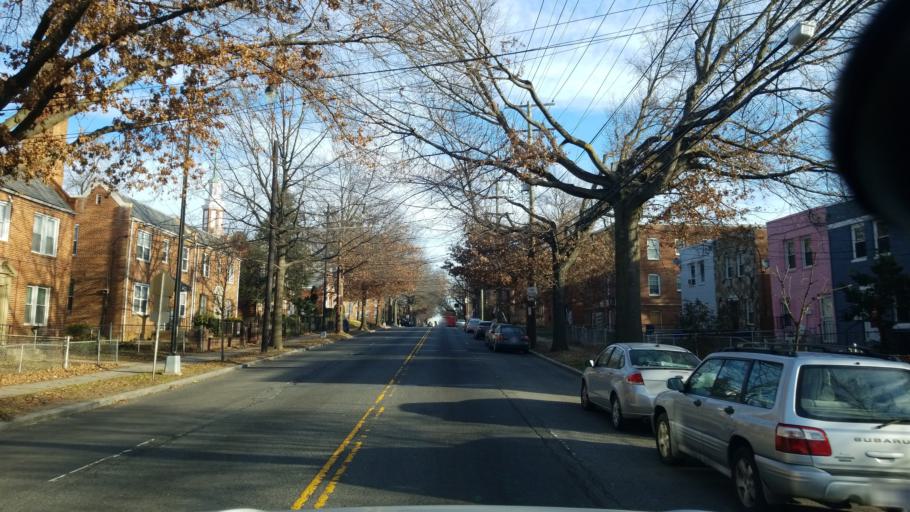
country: US
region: Maryland
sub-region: Prince George's County
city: Coral Hills
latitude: 38.8847
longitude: -76.9567
